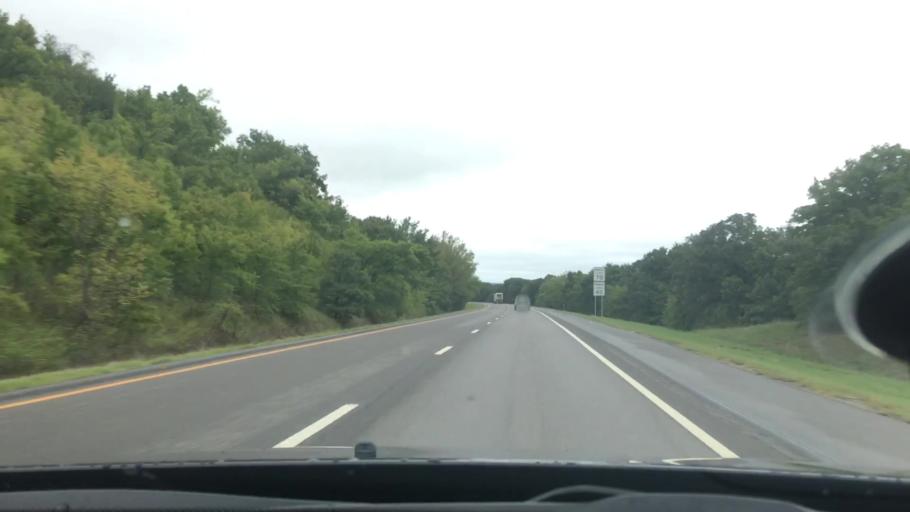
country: US
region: Oklahoma
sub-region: Okmulgee County
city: Morris
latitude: 35.4420
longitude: -95.7784
